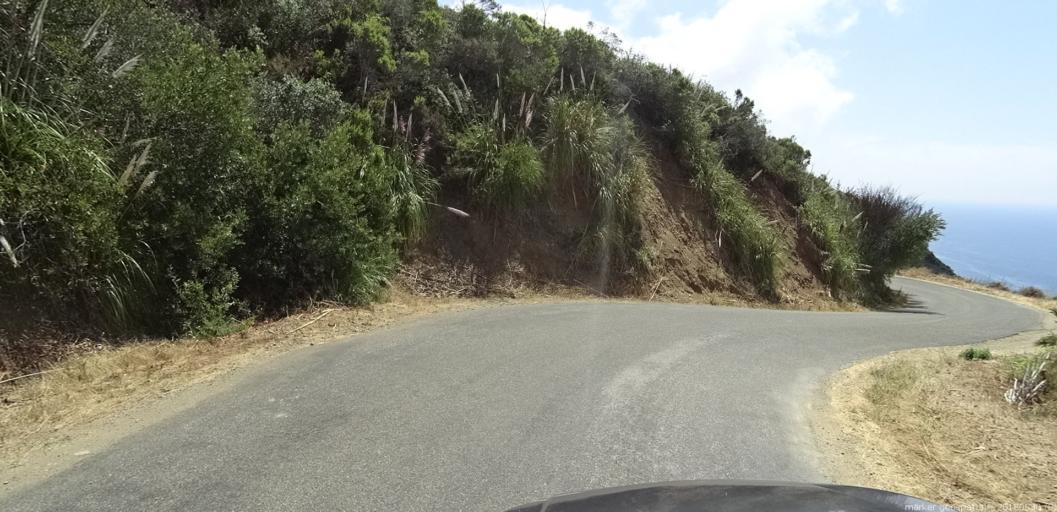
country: US
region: California
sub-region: Monterey County
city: Greenfield
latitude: 35.9926
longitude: -121.4893
